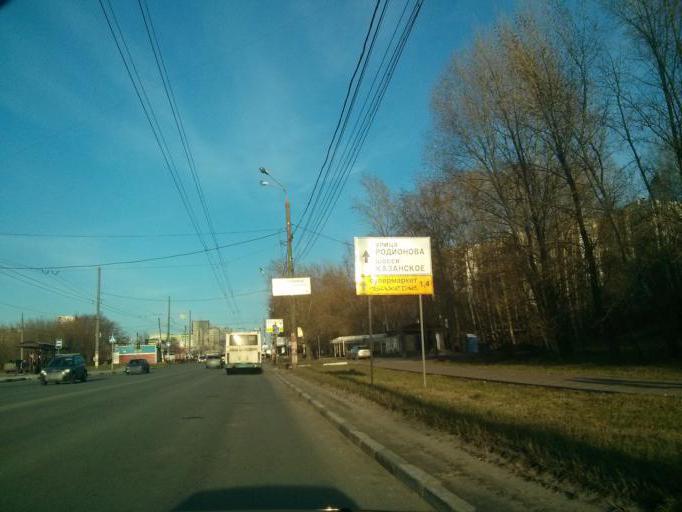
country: RU
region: Nizjnij Novgorod
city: Afonino
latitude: 56.2998
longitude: 44.0667
